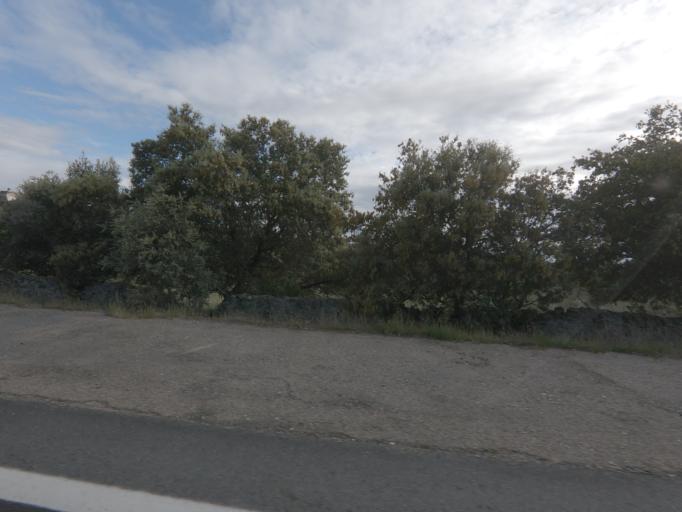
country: ES
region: Extremadura
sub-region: Provincia de Caceres
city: Huelaga
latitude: 40.0337
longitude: -6.6202
